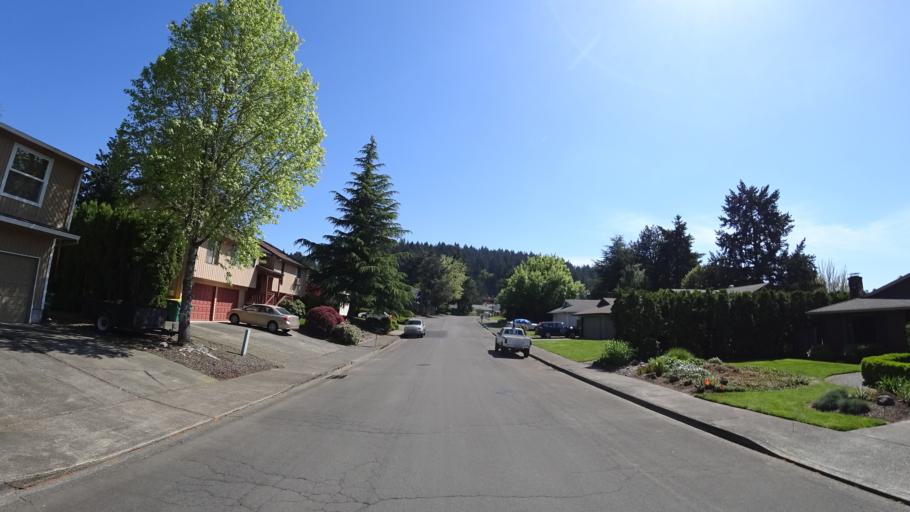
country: US
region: Oregon
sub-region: Washington County
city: Aloha
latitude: 45.4781
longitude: -122.8429
